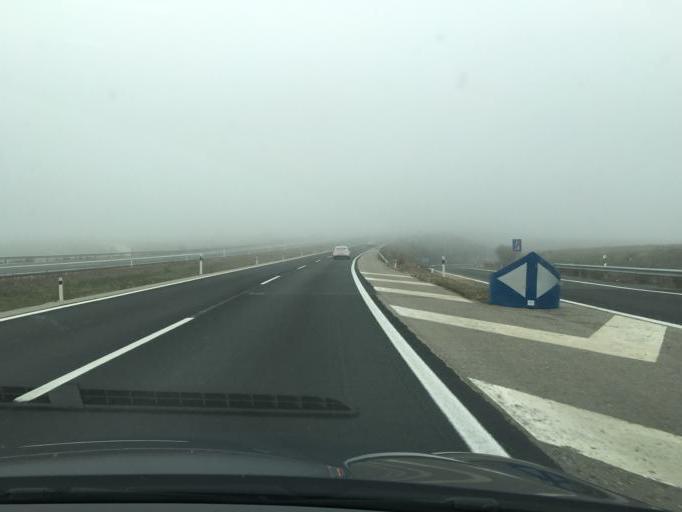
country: ES
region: Castille and Leon
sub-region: Provincia de Burgos
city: Pancorbo
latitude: 42.6251
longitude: -3.1112
